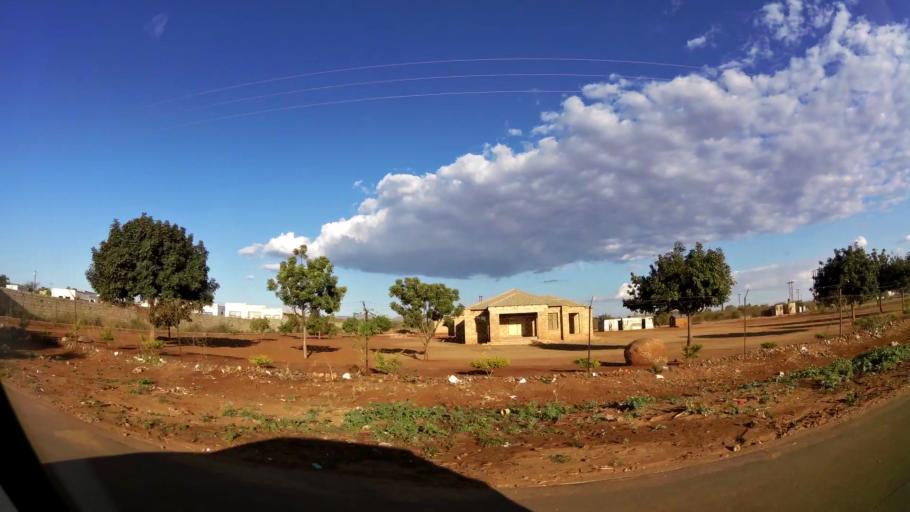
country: ZA
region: Limpopo
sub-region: Waterberg District Municipality
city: Mokopane
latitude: -24.1596
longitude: 28.9903
